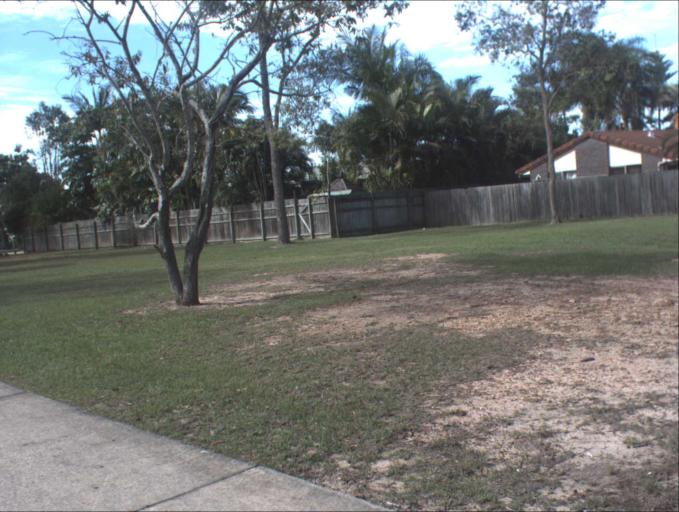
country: AU
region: Queensland
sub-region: Logan
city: Logan Reserve
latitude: -27.6903
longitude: 153.0786
